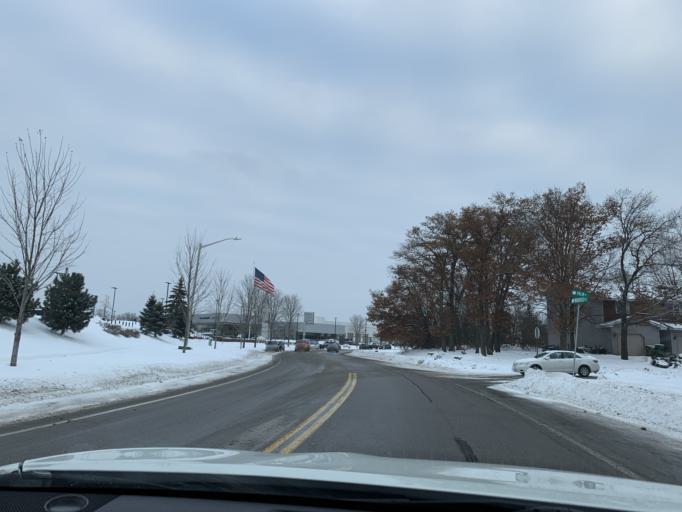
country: US
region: Minnesota
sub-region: Anoka County
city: Coon Rapids
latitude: 45.1612
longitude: -93.2879
